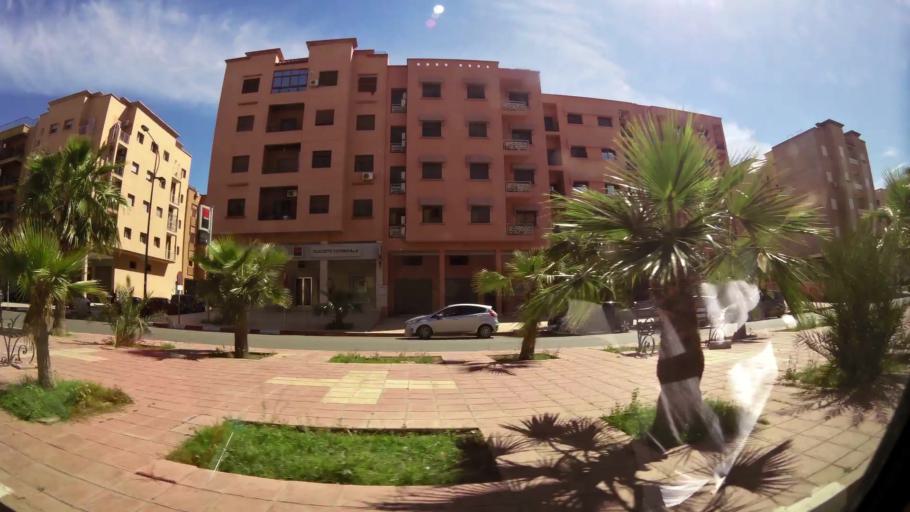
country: MA
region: Marrakech-Tensift-Al Haouz
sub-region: Marrakech
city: Marrakesh
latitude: 31.6732
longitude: -8.0196
